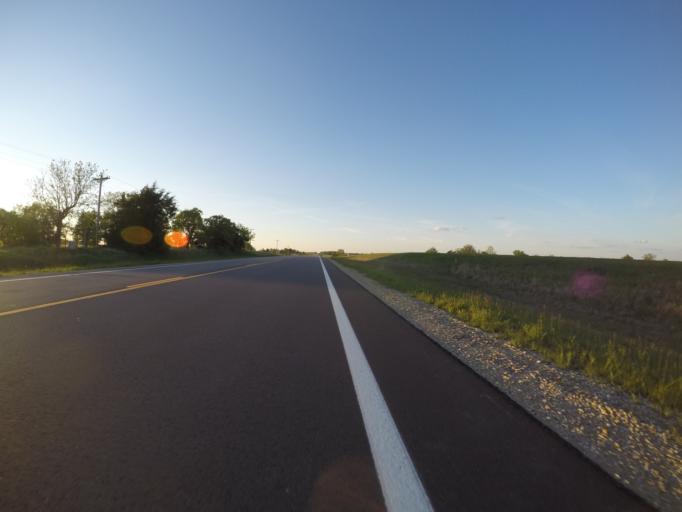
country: US
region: Kansas
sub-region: Pottawatomie County
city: Westmoreland
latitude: 39.3897
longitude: -96.5198
